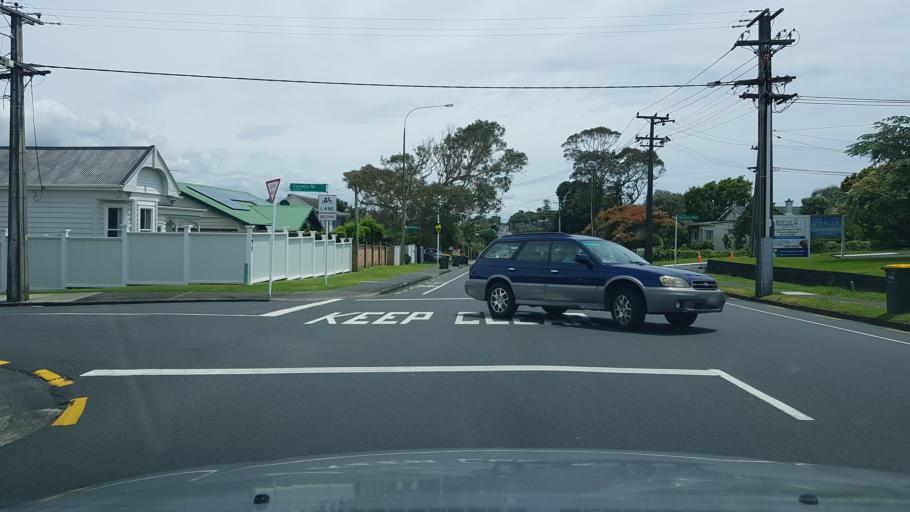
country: NZ
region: Auckland
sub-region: Auckland
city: North Shore
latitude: -36.8065
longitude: 174.7893
